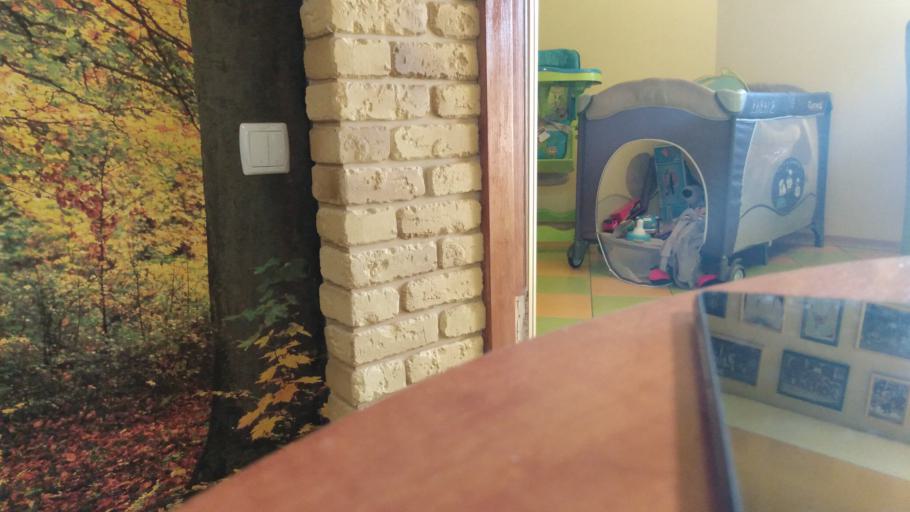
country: RU
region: Tverskaya
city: Bologoye
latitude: 57.9476
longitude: 34.1701
